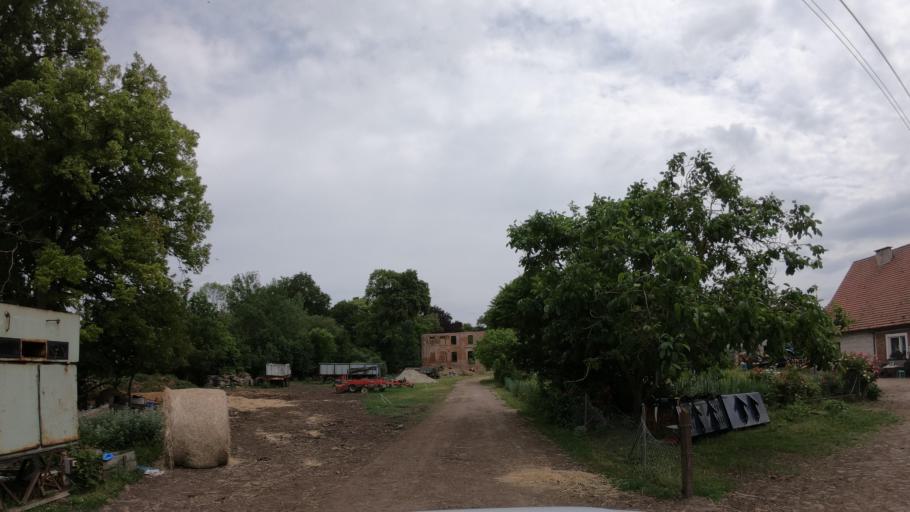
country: PL
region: West Pomeranian Voivodeship
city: Trzcinsko Zdroj
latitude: 52.9461
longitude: 14.7261
